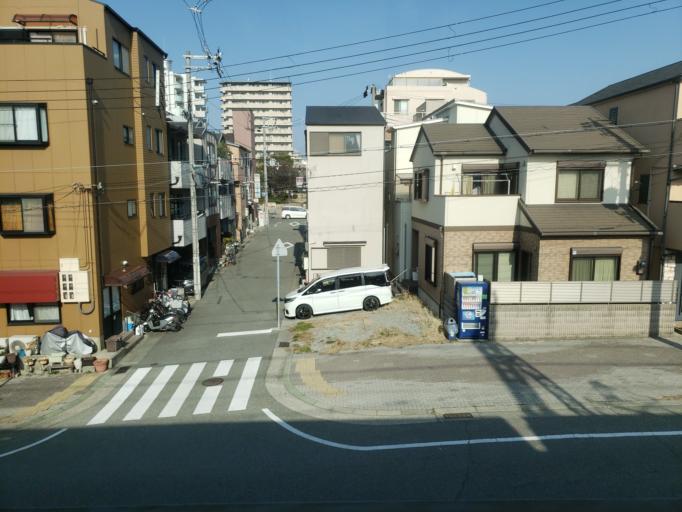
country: JP
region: Hyogo
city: Kobe
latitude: 34.6550
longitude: 135.1399
